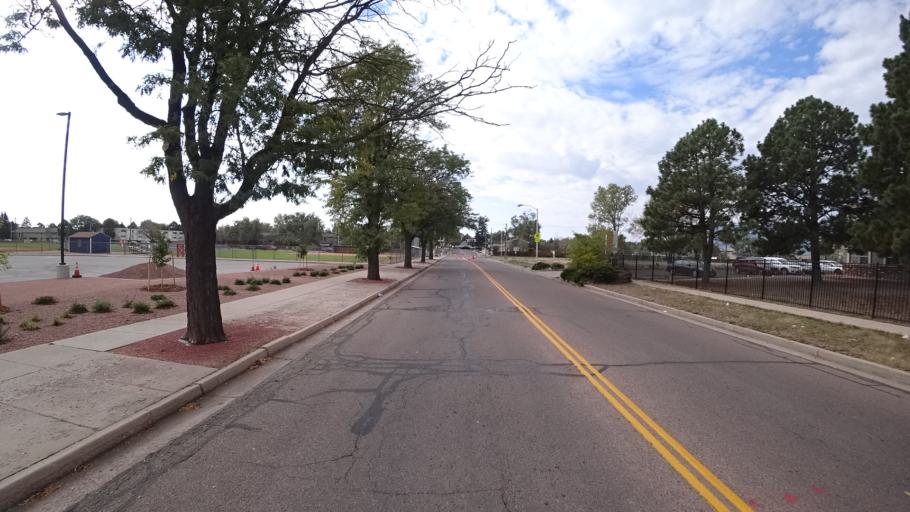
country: US
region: Colorado
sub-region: El Paso County
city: Cimarron Hills
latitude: 38.8482
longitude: -104.7527
